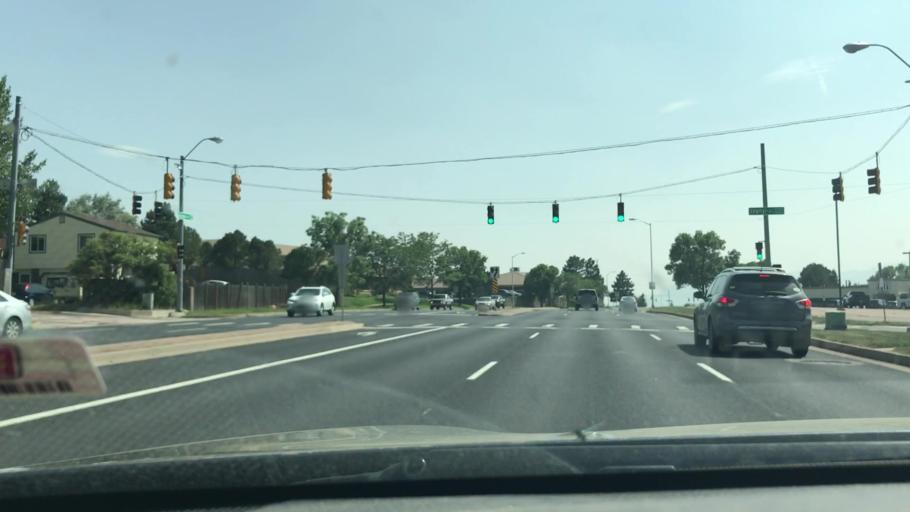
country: US
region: Colorado
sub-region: El Paso County
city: Black Forest
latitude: 38.9446
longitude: -104.7743
